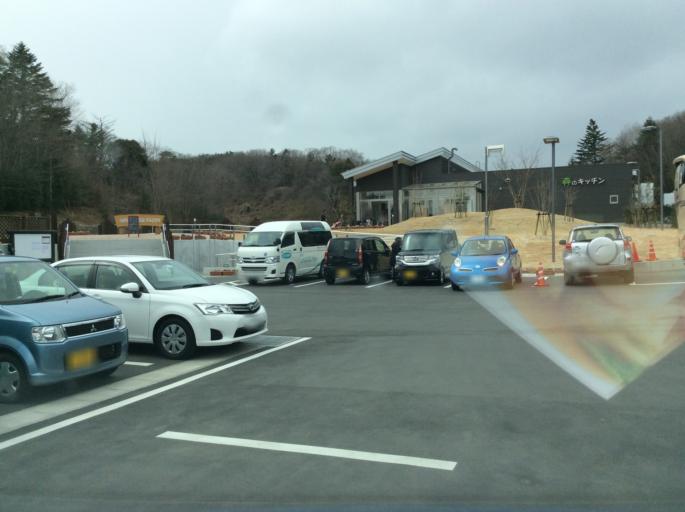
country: JP
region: Fukushima
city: Iwaki
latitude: 37.1241
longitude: 140.9472
